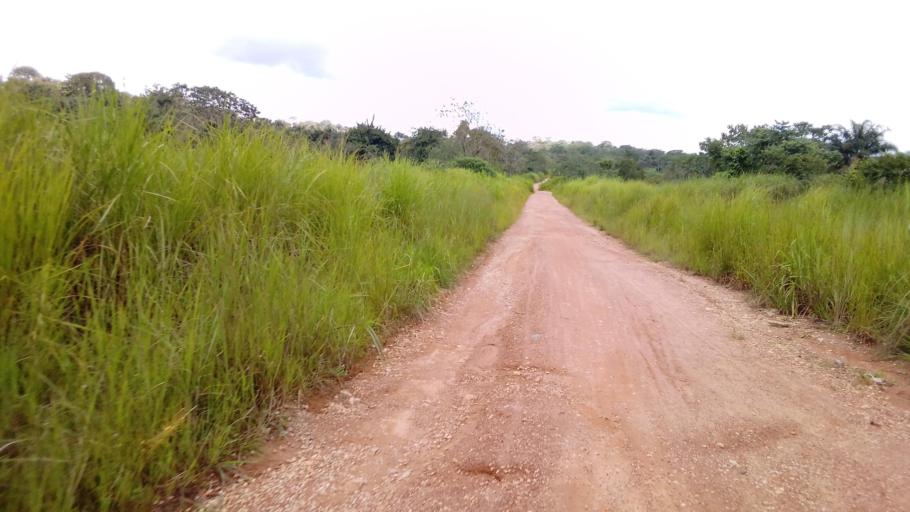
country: SL
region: Eastern Province
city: Koidu
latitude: 8.6815
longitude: -10.9718
